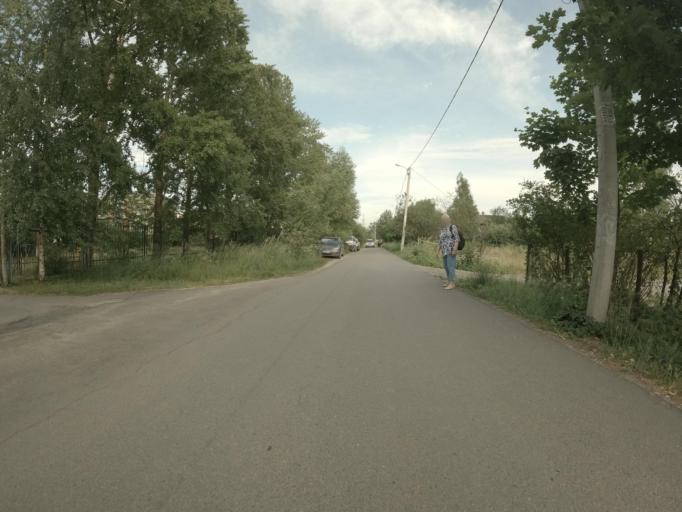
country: RU
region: St.-Petersburg
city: Krasnogvargeisky
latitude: 59.9364
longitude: 30.5158
